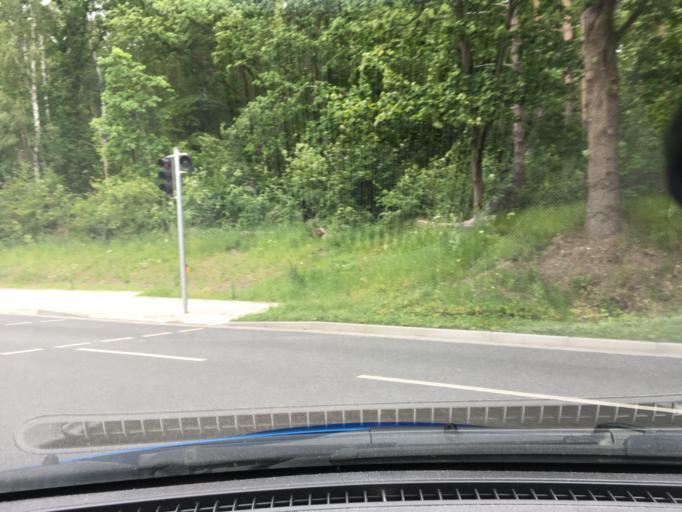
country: DE
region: Schleswig-Holstein
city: Kroppelshagen-Fahrendorf
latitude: 53.4547
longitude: 10.3493
